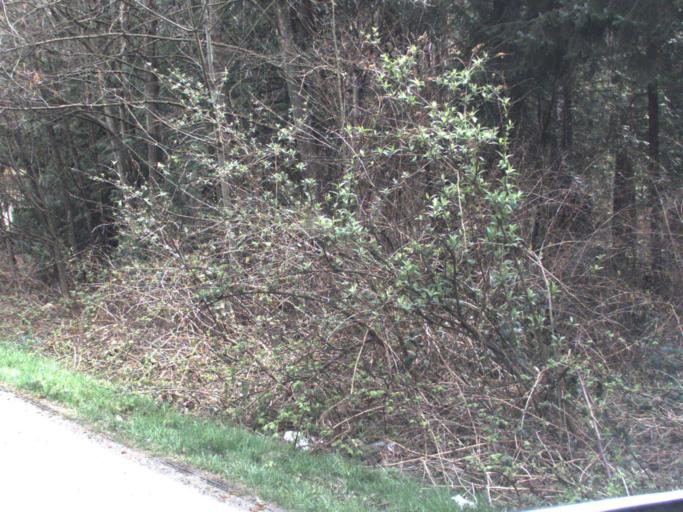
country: US
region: Washington
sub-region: King County
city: Maple Valley
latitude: 47.3580
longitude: -122.0414
